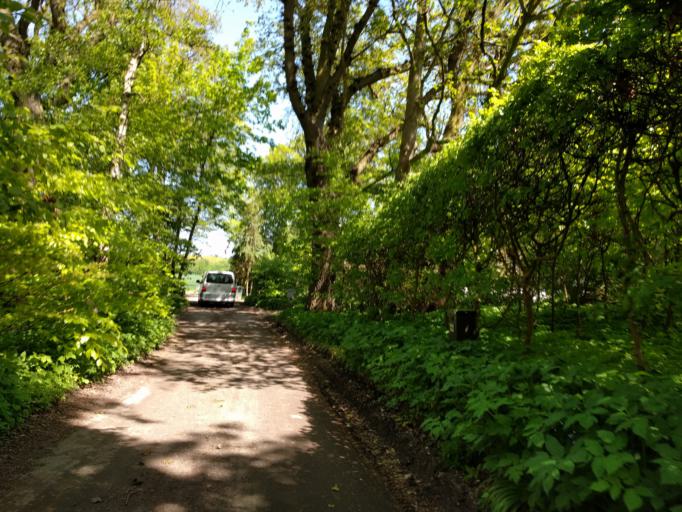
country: DK
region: Zealand
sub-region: Guldborgsund Kommune
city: Stubbekobing
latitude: 54.7555
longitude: 12.0376
